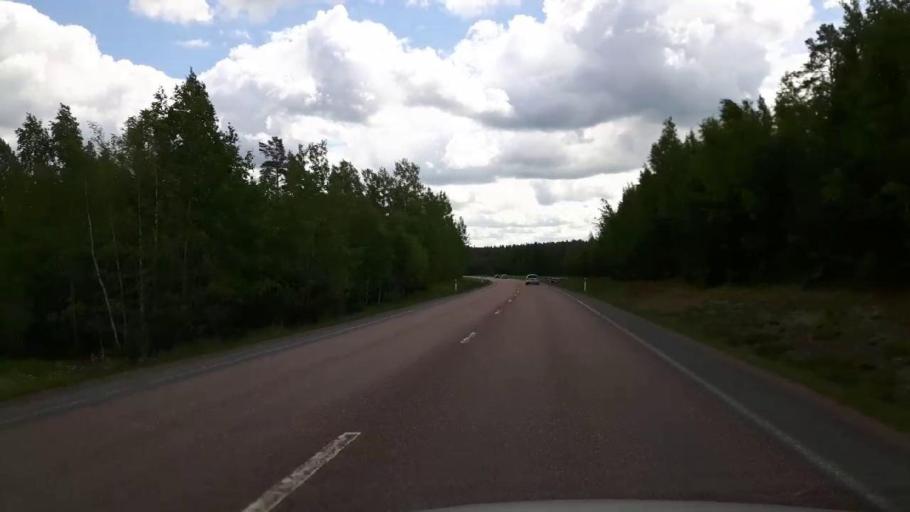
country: SE
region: Dalarna
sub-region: Faluns Kommun
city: Falun
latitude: 60.5038
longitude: 15.7416
